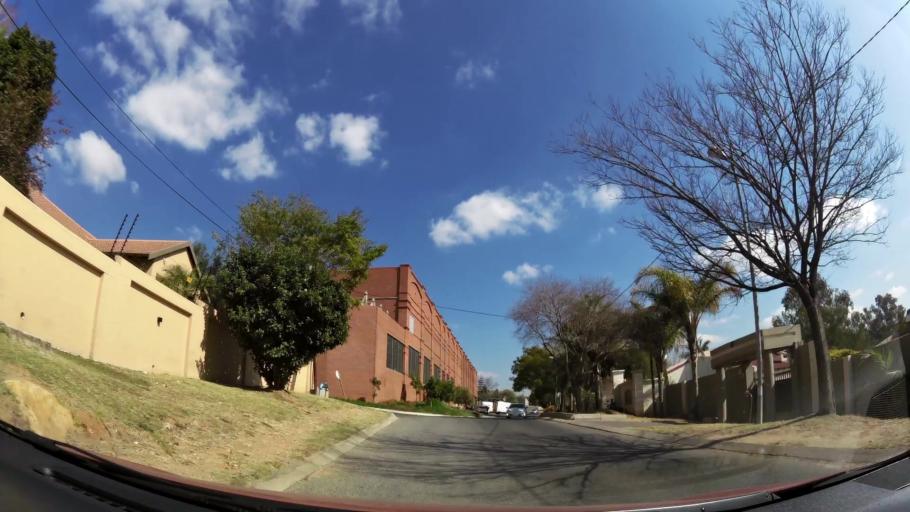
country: ZA
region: Gauteng
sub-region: City of Johannesburg Metropolitan Municipality
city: Roodepoort
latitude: -26.0847
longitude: 27.9481
